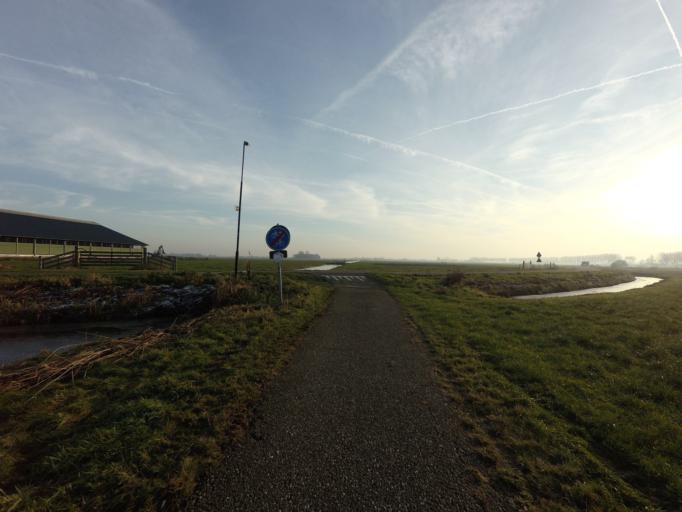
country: NL
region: Utrecht
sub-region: Gemeente De Ronde Venen
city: Mijdrecht
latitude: 52.1777
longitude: 4.9084
